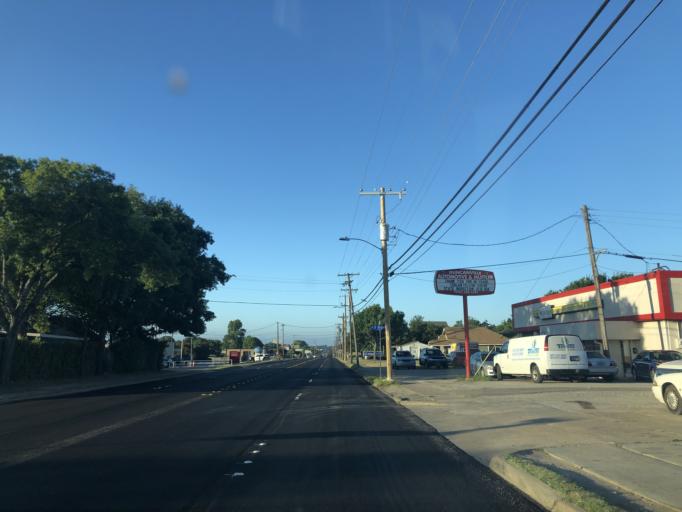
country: US
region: Texas
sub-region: Dallas County
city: Duncanville
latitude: 32.6430
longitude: -96.9085
